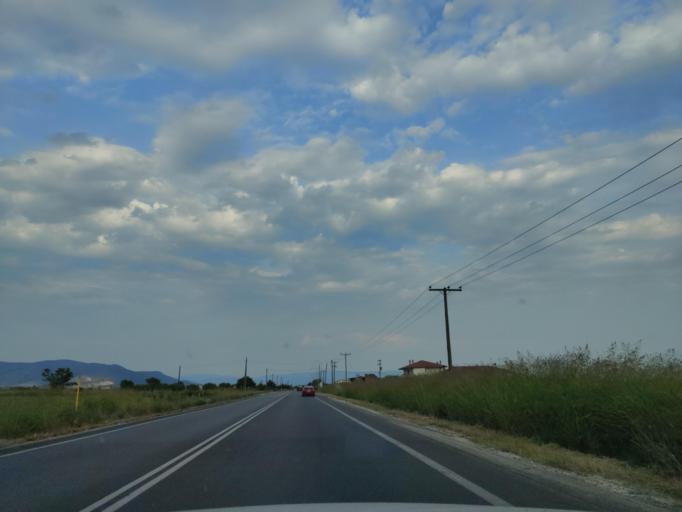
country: GR
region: East Macedonia and Thrace
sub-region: Nomos Dramas
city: Xiropotamos
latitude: 41.1612
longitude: 24.0821
